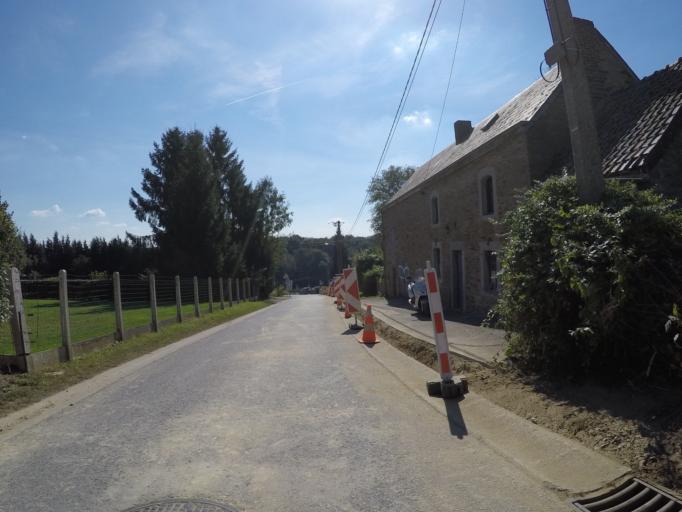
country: BE
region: Wallonia
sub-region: Province de Namur
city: Assesse
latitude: 50.3335
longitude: 5.0329
